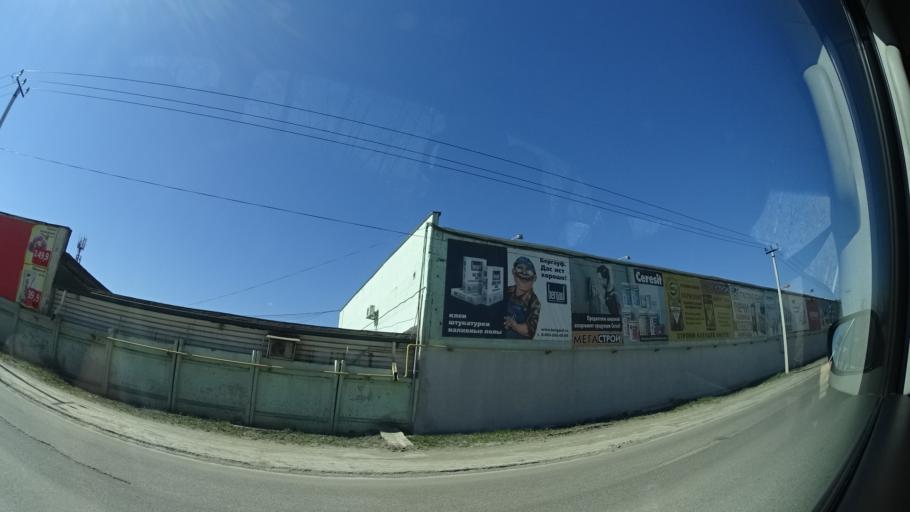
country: RU
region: Perm
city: Perm
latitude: 58.0878
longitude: 56.3112
